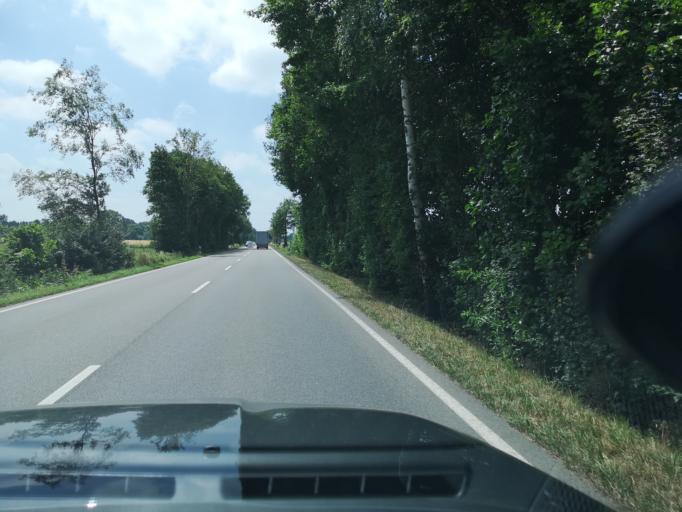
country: DE
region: North Rhine-Westphalia
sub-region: Regierungsbezirk Munster
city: Isselburg
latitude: 51.8350
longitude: 6.4521
